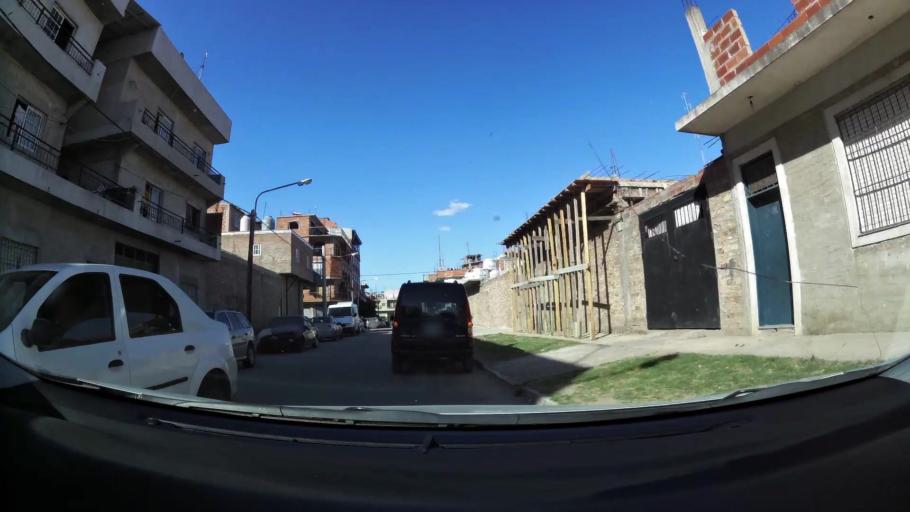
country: AR
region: Buenos Aires F.D.
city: Villa Lugano
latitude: -34.7041
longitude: -58.4820
